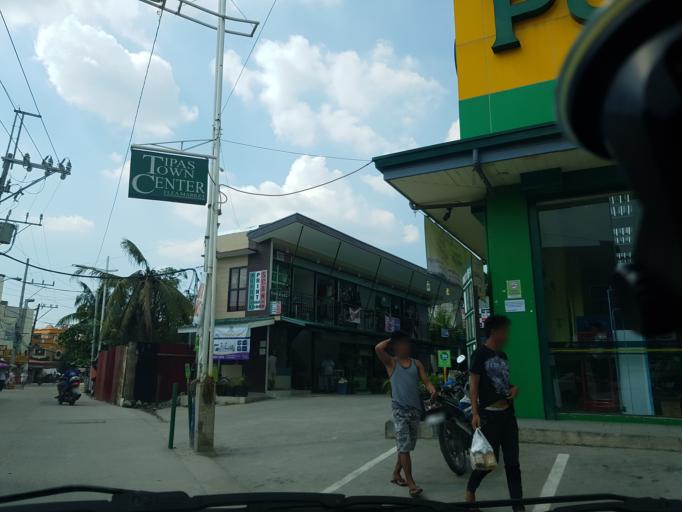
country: PH
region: Calabarzon
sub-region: Province of Rizal
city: Pateros
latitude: 14.5465
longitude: 121.0828
